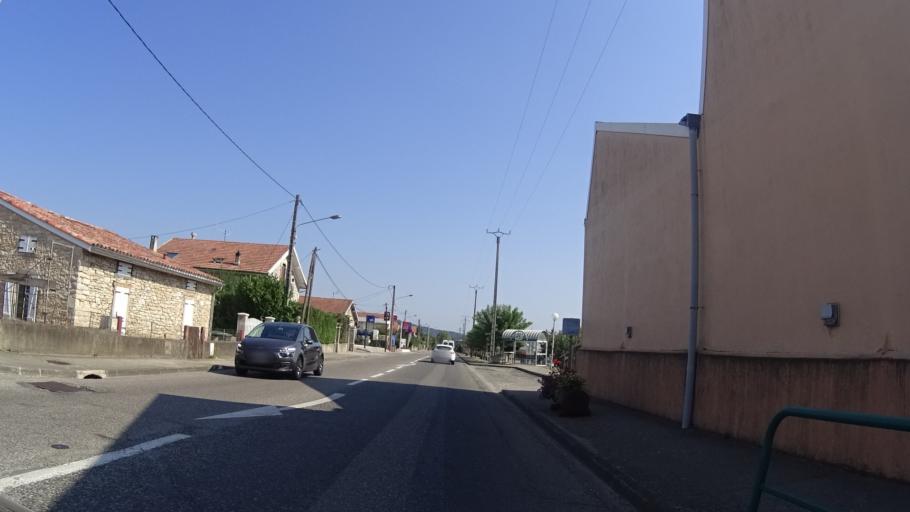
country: FR
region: Midi-Pyrenees
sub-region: Departement de l'Ariege
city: Lavelanet
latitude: 42.9724
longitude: 1.8670
